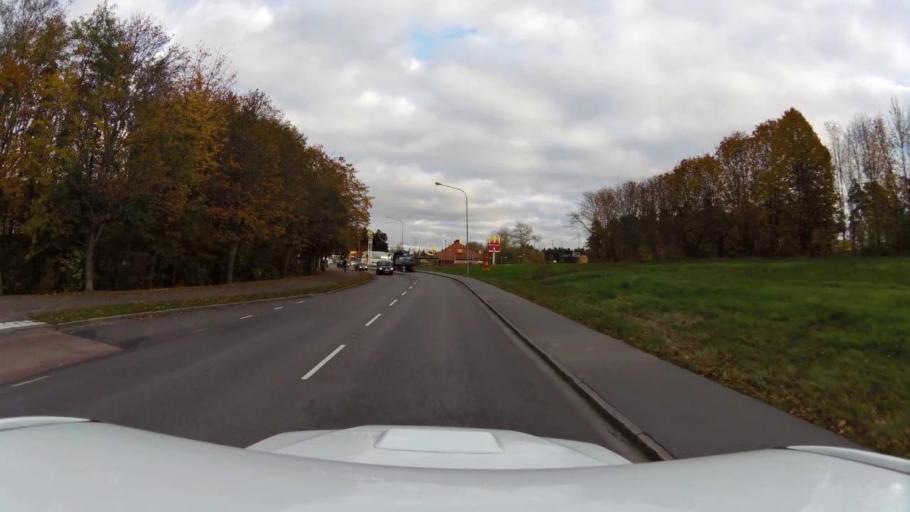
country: SE
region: OEstergoetland
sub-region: Linkopings Kommun
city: Linkoping
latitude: 58.4061
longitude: 15.5759
